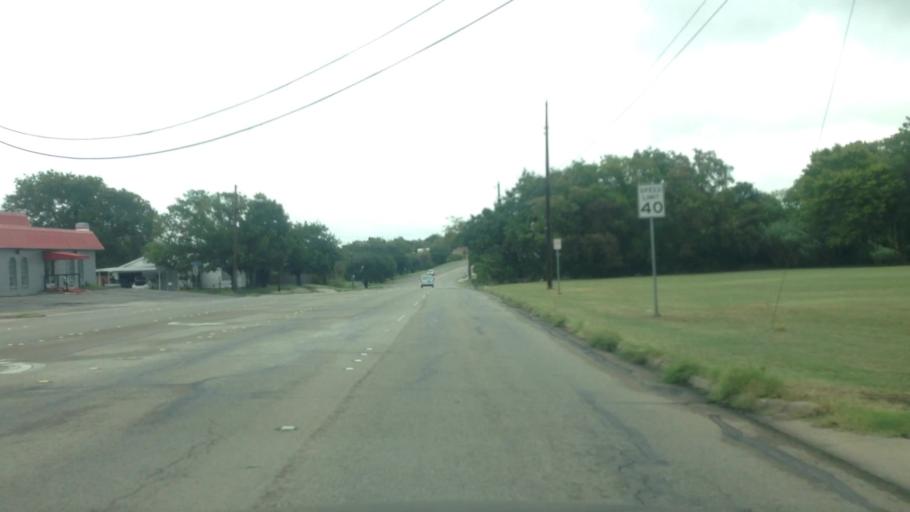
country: US
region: Texas
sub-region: Tarrant County
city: White Settlement
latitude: 32.7661
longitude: -97.4679
